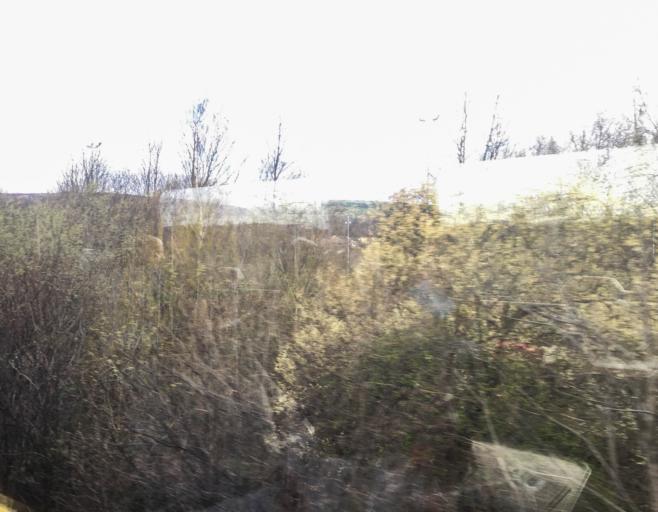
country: GB
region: Scotland
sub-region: West Dunbartonshire
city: Old Kilpatrick
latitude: 55.9184
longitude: -4.4418
